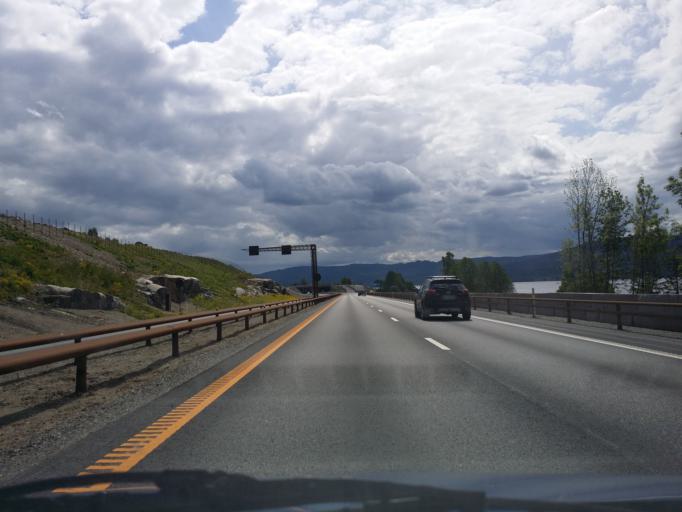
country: NO
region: Hedmark
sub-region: Stange
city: Stange
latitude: 60.5689
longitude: 11.2609
